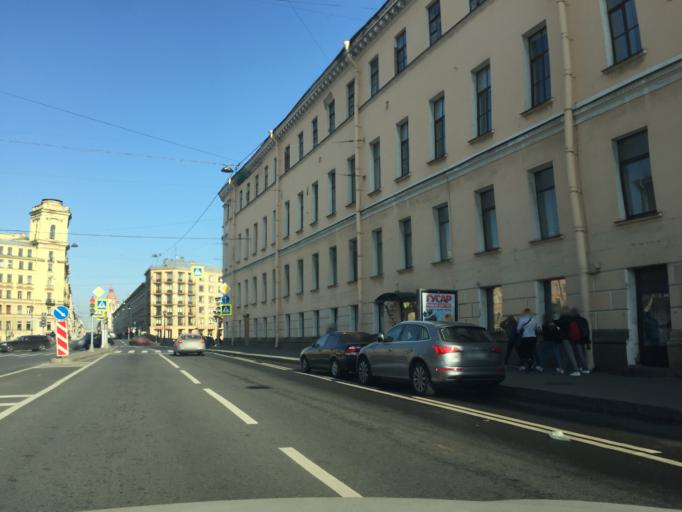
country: RU
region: St.-Petersburg
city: Saint Petersburg
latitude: 59.9183
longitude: 30.3078
